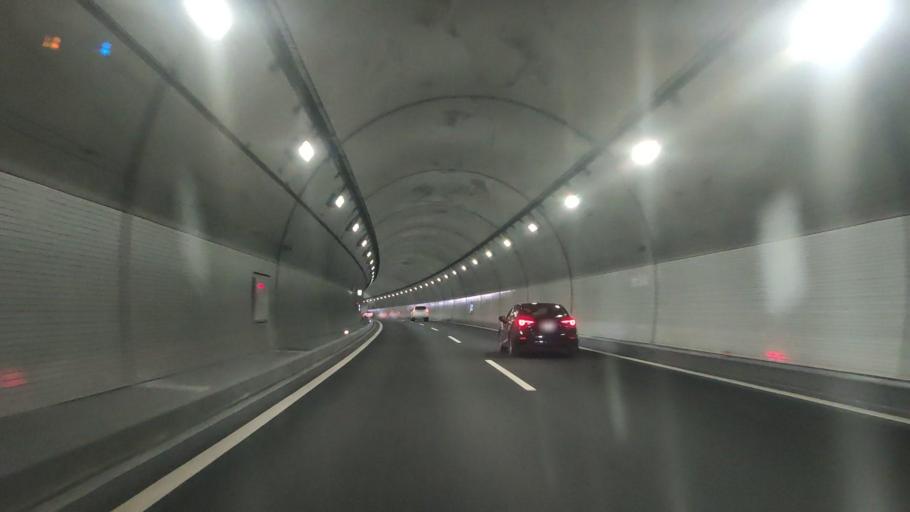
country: JP
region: Fukuoka
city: Kanda
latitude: 33.8038
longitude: 130.9423
